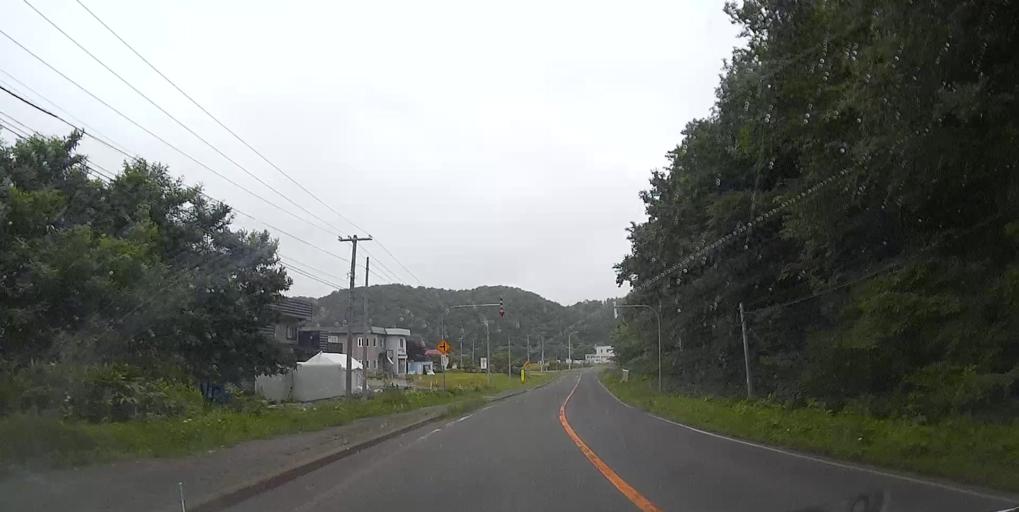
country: JP
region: Hokkaido
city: Iwanai
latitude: 42.4347
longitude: 139.9981
